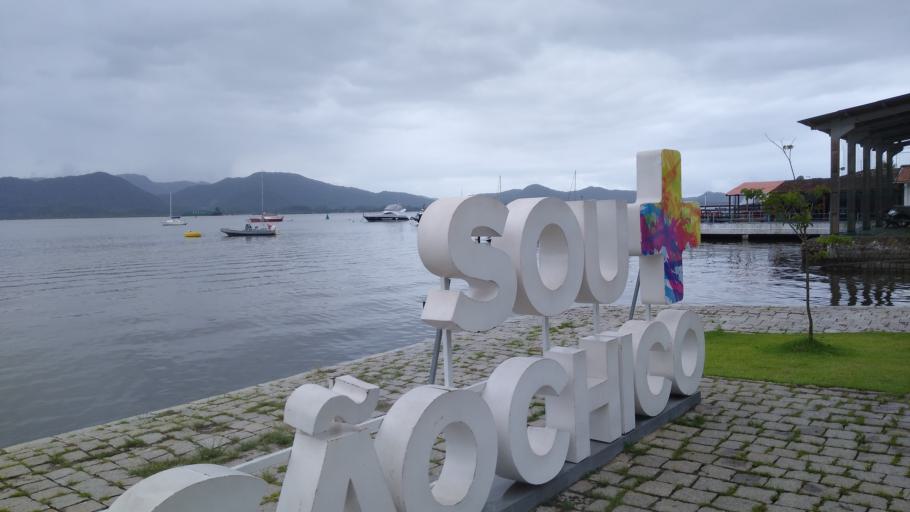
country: BR
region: Santa Catarina
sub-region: Sao Francisco Do Sul
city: Sao Francisco do Sul
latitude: -26.2451
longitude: -48.6406
